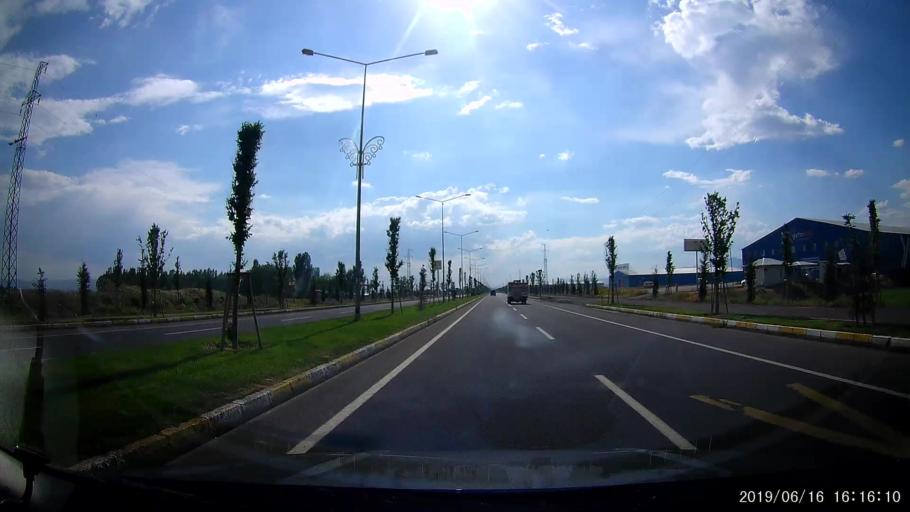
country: TR
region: Erzurum
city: Erzurum
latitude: 39.9626
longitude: 41.2114
